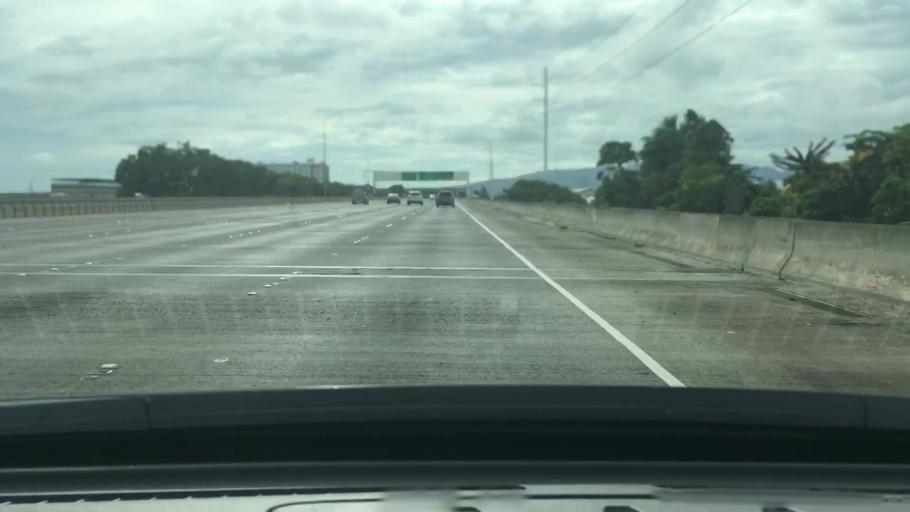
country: US
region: Hawaii
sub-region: Honolulu County
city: Halawa Heights
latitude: 21.3363
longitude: -157.9073
